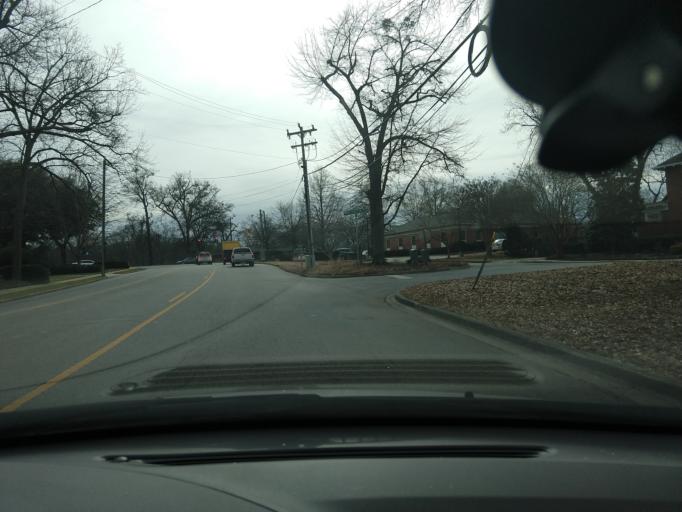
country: US
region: South Carolina
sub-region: Spartanburg County
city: Spartanburg
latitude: 34.9579
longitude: -81.9121
